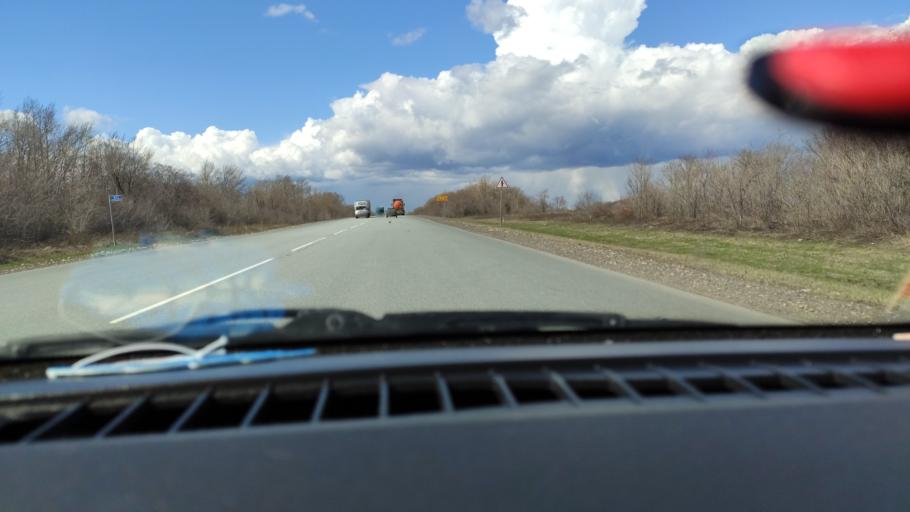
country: RU
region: Samara
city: Obsharovka
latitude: 53.2172
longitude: 48.7630
